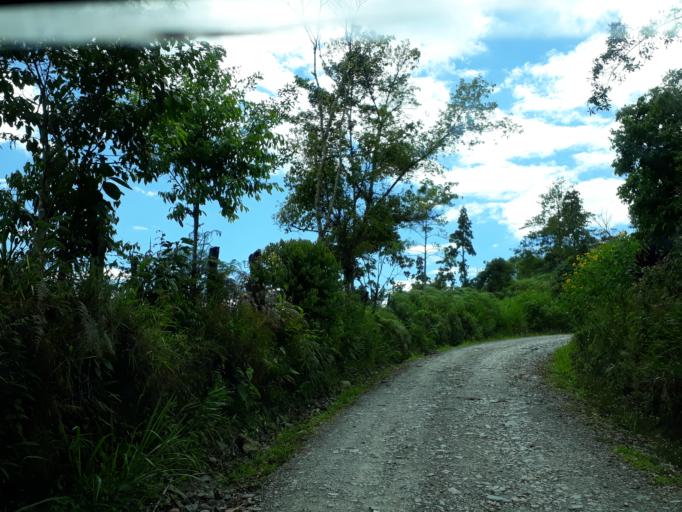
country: CO
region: Cundinamarca
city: Topaipi
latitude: 5.3460
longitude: -74.1896
